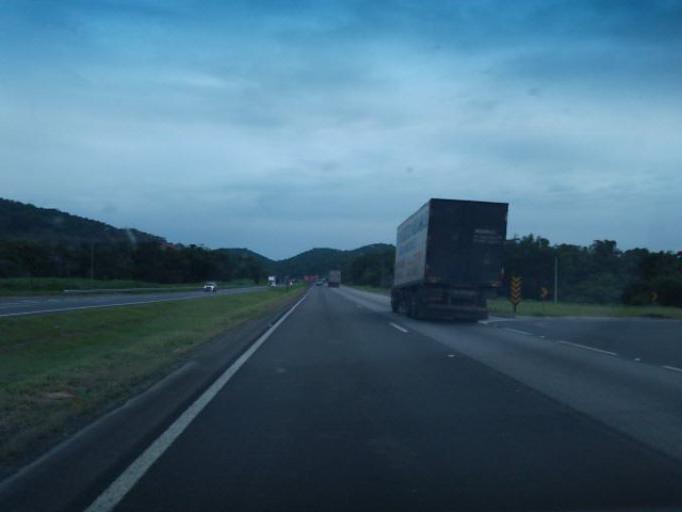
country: BR
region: Sao Paulo
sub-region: Juquia
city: Juquia
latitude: -24.3418
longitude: -47.6464
